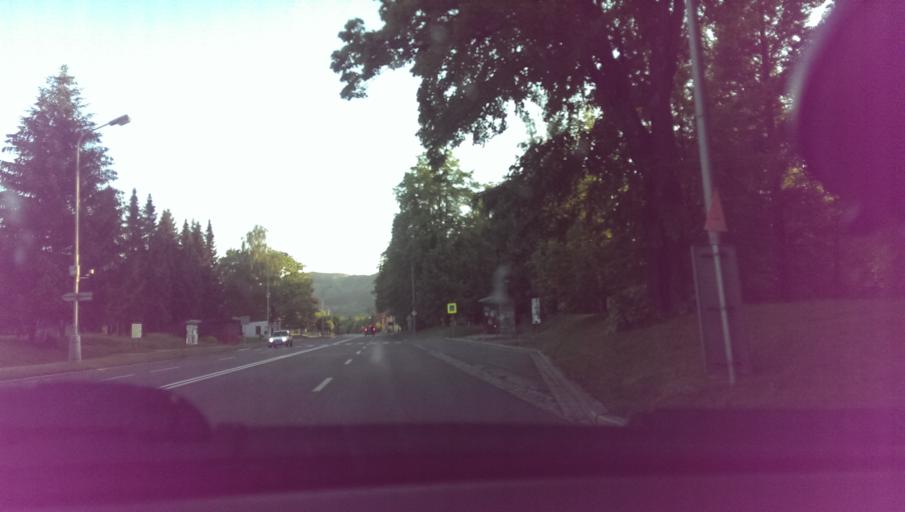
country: CZ
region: Moravskoslezsky
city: Frenstat pod Radhostem
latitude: 49.5430
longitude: 18.2084
